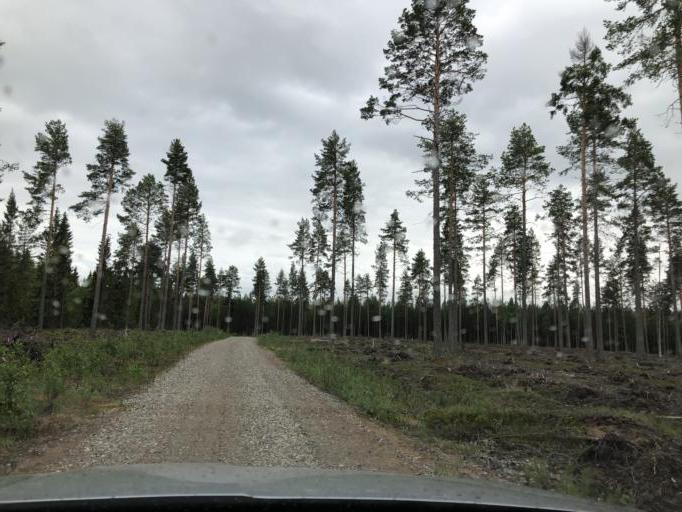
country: SE
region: Norrbotten
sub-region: Pitea Kommun
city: Roknas
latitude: 65.3984
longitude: 21.2698
